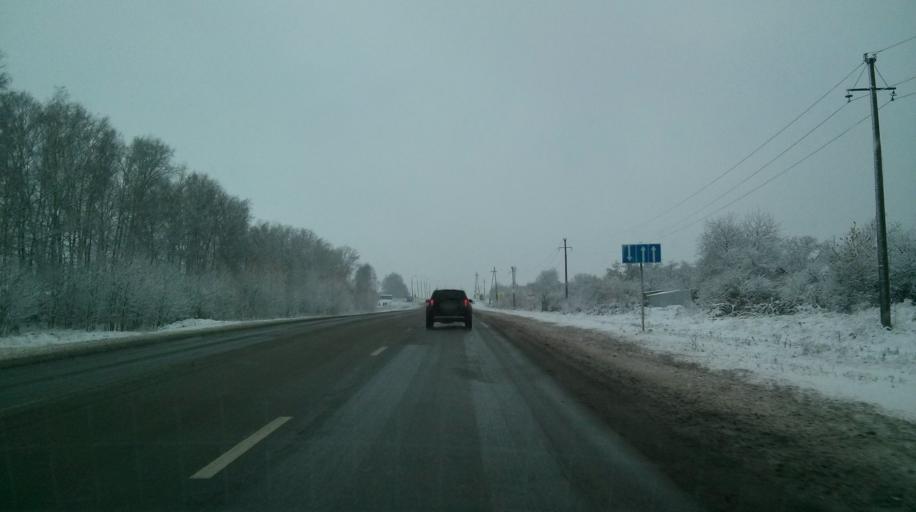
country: RU
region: Nizjnij Novgorod
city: Burevestnik
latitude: 56.1810
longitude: 43.7896
